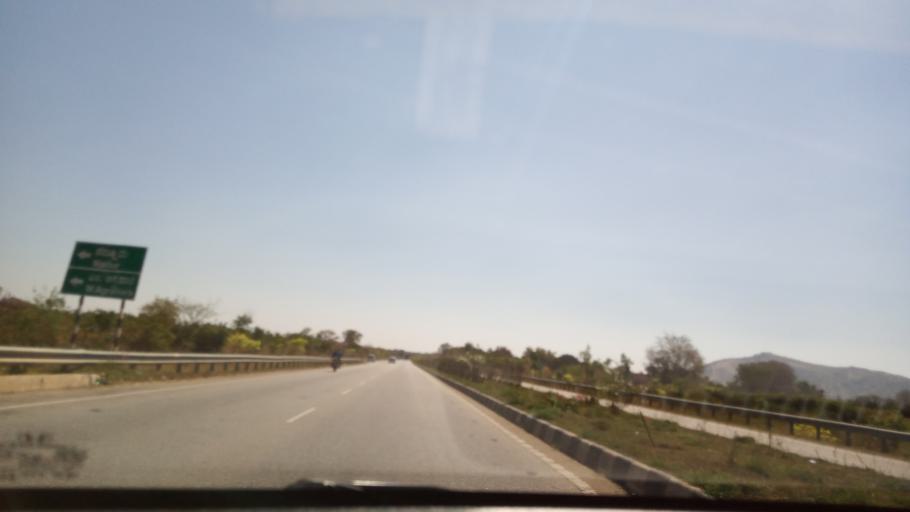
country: IN
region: Karnataka
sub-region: Kolar
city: Mulbagal
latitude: 13.1472
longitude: 78.2650
